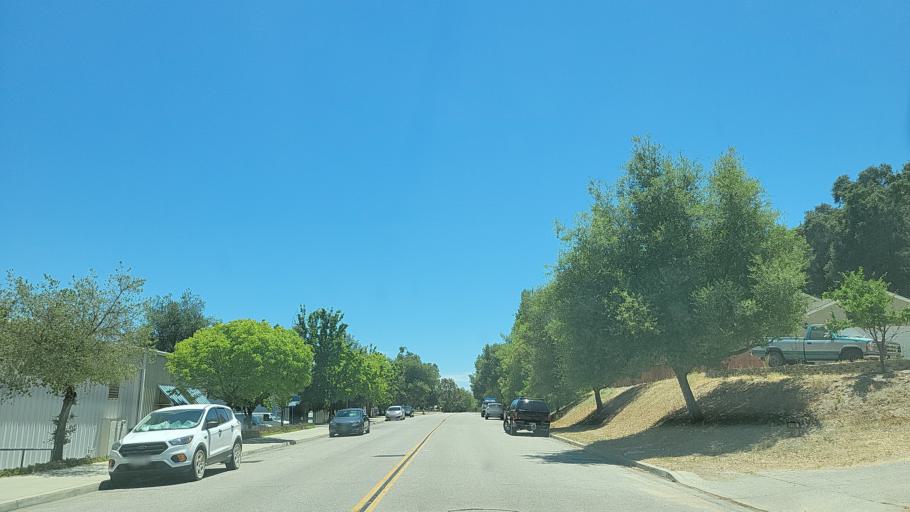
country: US
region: California
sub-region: San Luis Obispo County
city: Atascadero
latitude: 35.5104
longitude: -120.6713
